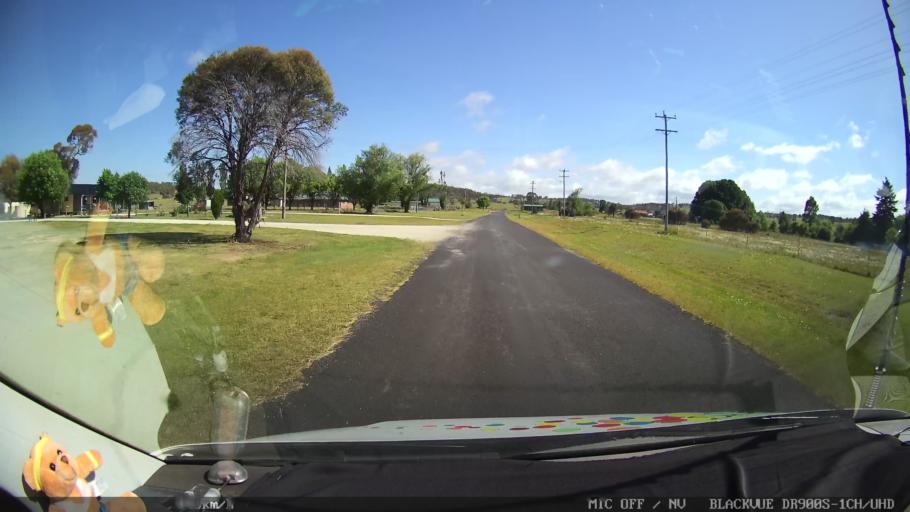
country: AU
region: New South Wales
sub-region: Guyra
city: Guyra
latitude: -30.1311
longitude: 151.6829
